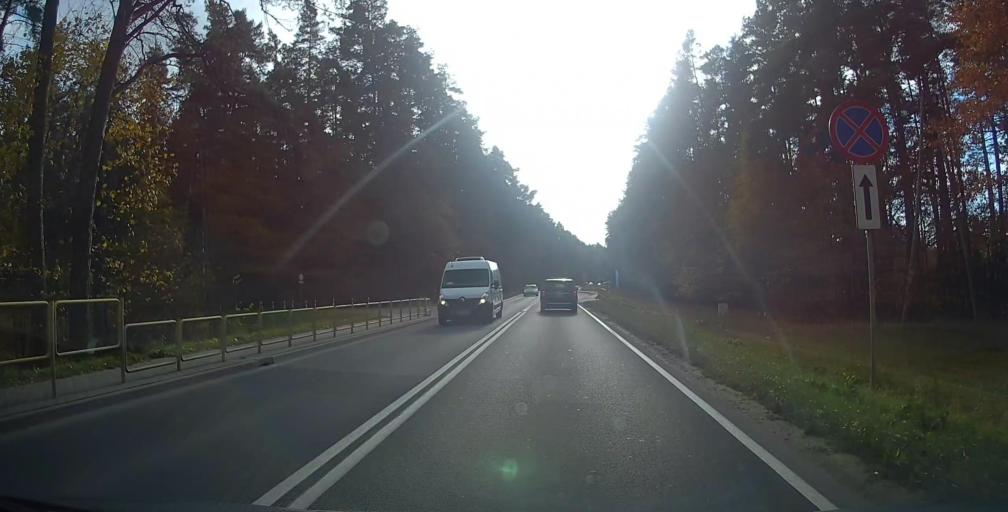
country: PL
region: Warmian-Masurian Voivodeship
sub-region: Powiat elcki
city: Elk
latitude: 53.7876
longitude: 22.3523
